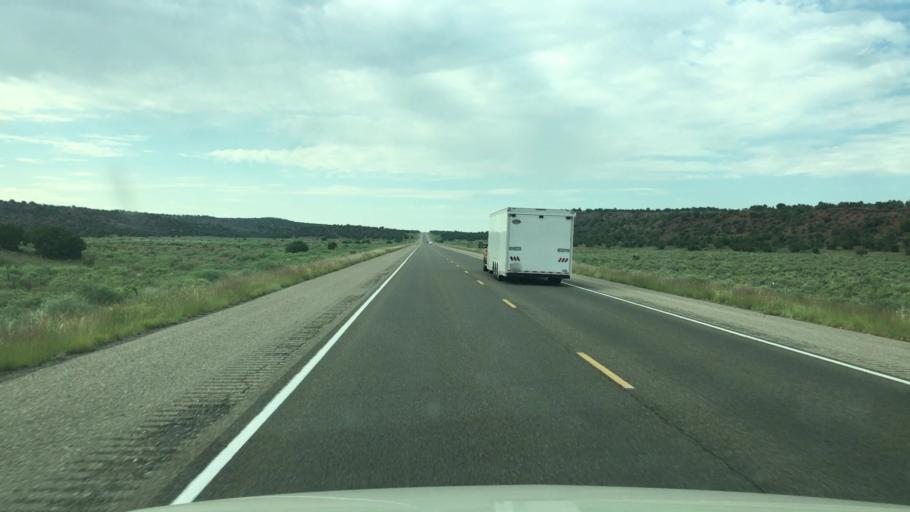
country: US
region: New Mexico
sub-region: Santa Fe County
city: Eldorado at Santa Fe
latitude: 35.2459
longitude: -105.8065
